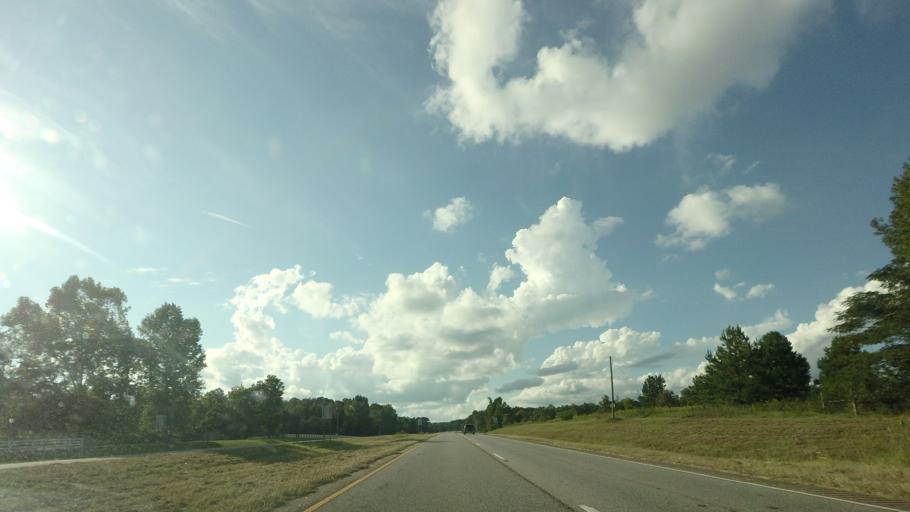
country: US
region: Georgia
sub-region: Houston County
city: Perry
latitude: 32.3659
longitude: -83.6077
